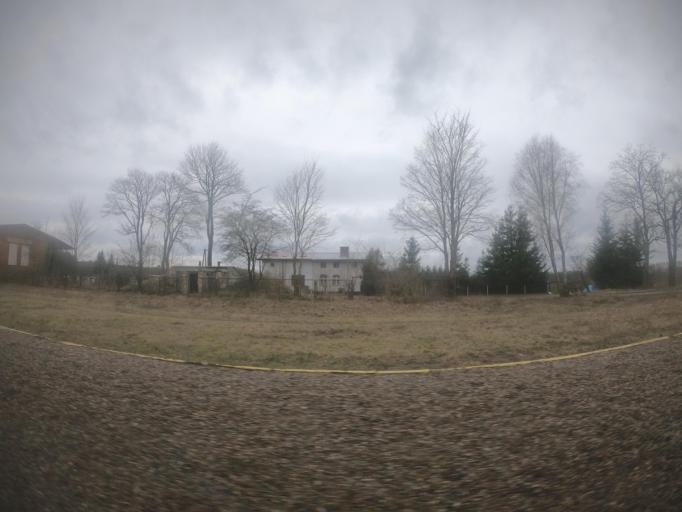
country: PL
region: West Pomeranian Voivodeship
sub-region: Powiat szczecinecki
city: Bialy Bor
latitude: 53.8074
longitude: 16.8664
